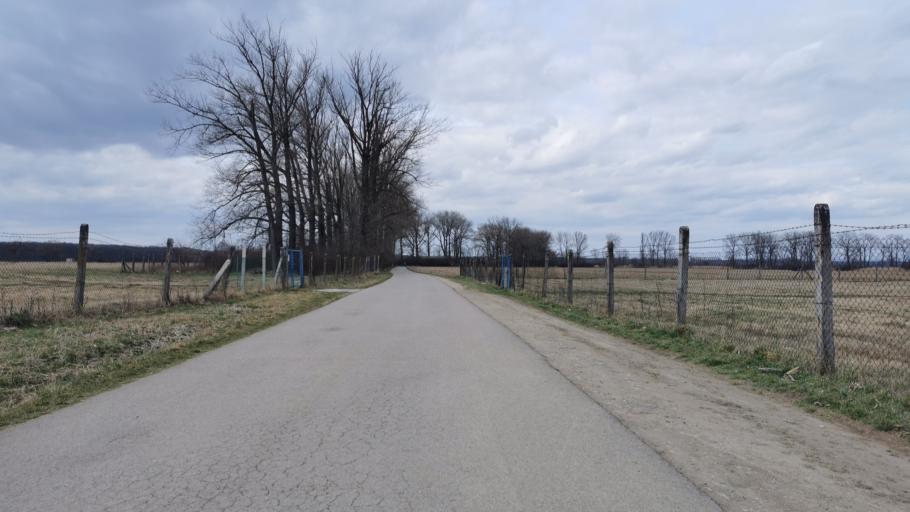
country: SK
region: Trnavsky
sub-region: Okres Skalica
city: Skalica
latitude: 48.8574
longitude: 17.2248
